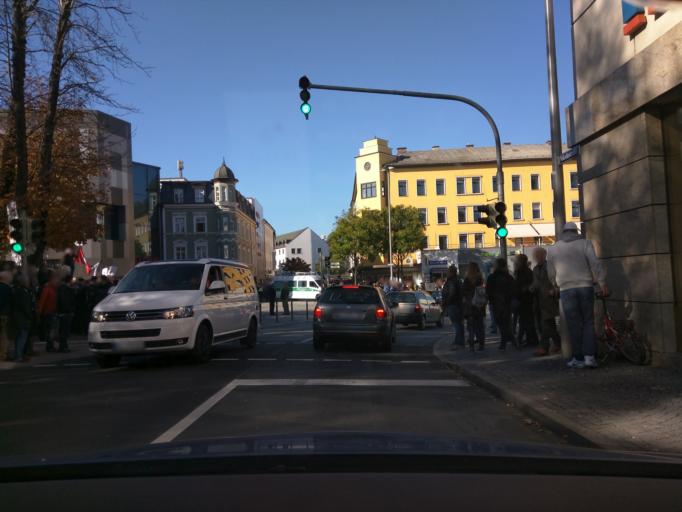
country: DE
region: Bavaria
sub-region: Lower Bavaria
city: Passau
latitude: 48.5734
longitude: 13.4577
